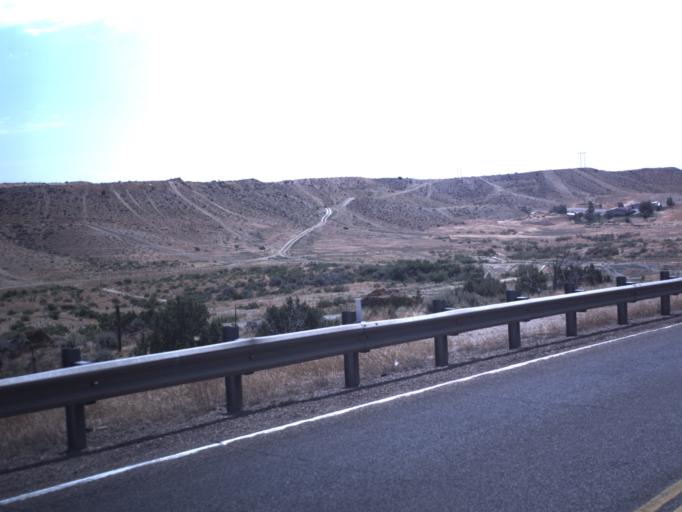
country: US
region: Utah
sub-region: Uintah County
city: Vernal
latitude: 40.5107
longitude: -109.5239
